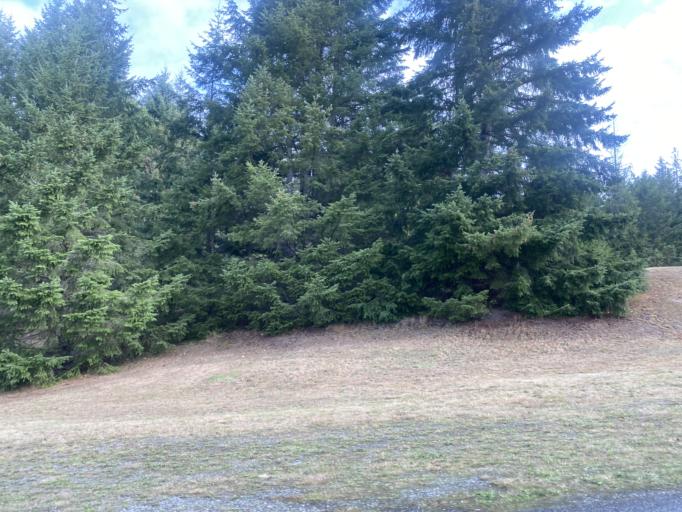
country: US
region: Washington
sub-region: Island County
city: Langley
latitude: 48.0095
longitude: -122.4061
